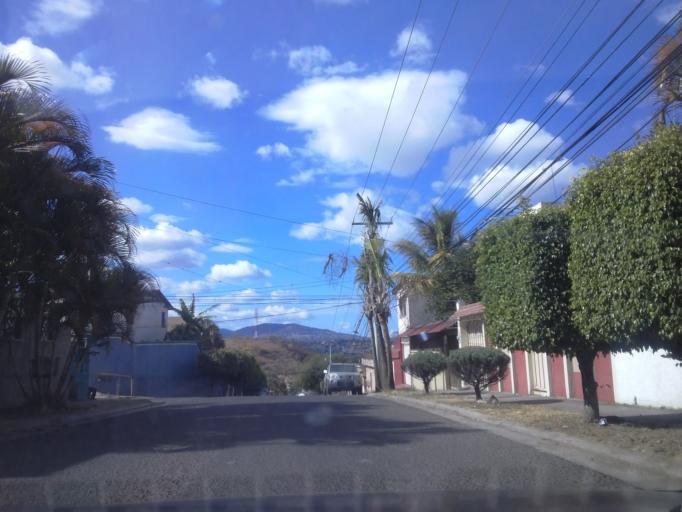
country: HN
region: Francisco Morazan
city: Yaguacire
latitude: 14.0458
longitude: -87.2327
